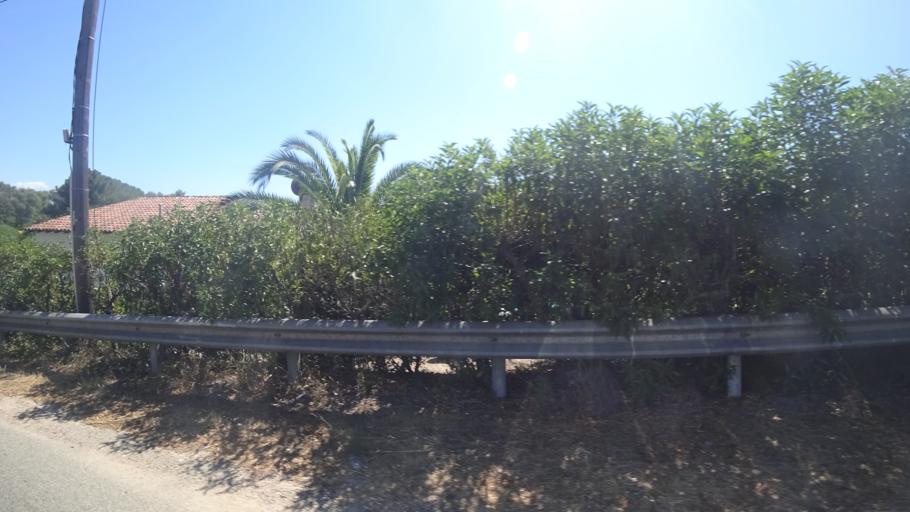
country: FR
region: Corsica
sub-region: Departement de la Corse-du-Sud
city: Ajaccio
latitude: 41.9480
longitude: 8.7347
